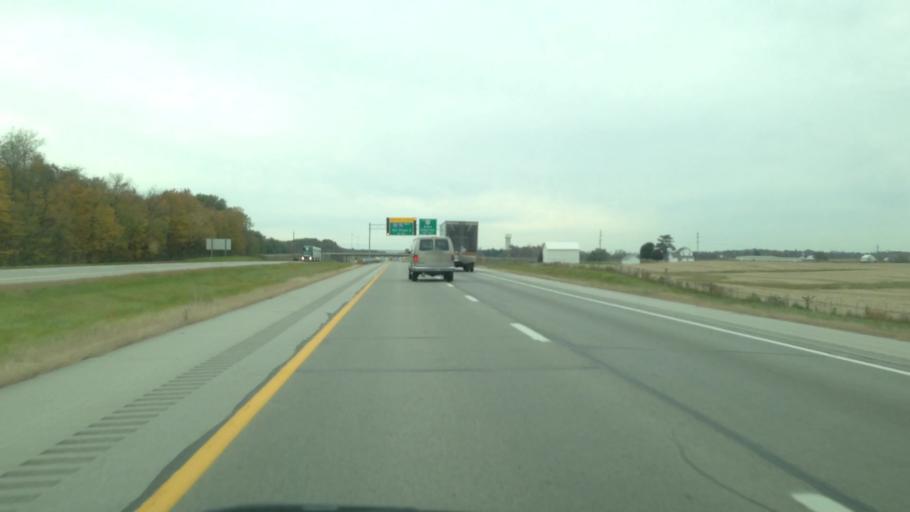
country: US
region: Ohio
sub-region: Williams County
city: Montpelier
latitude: 41.6286
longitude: -84.7403
